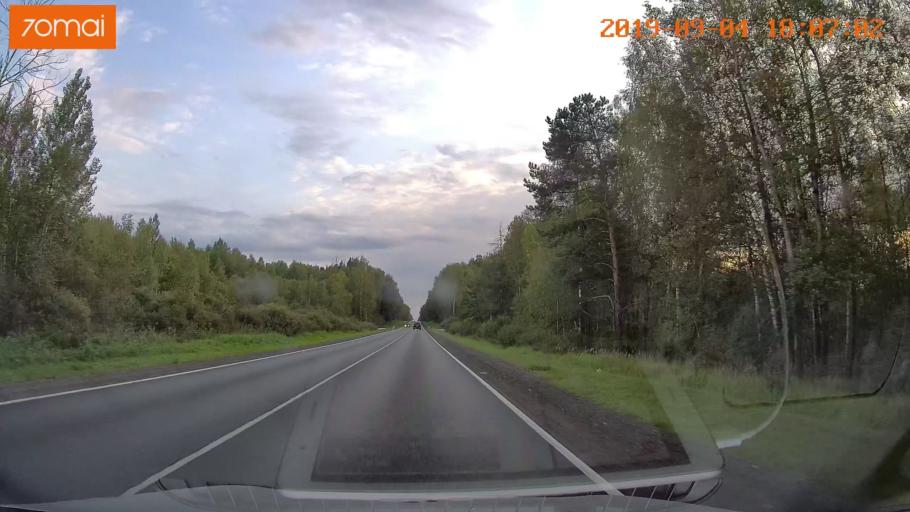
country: RU
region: Moskovskaya
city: Khorlovo
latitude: 55.4243
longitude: 38.8069
